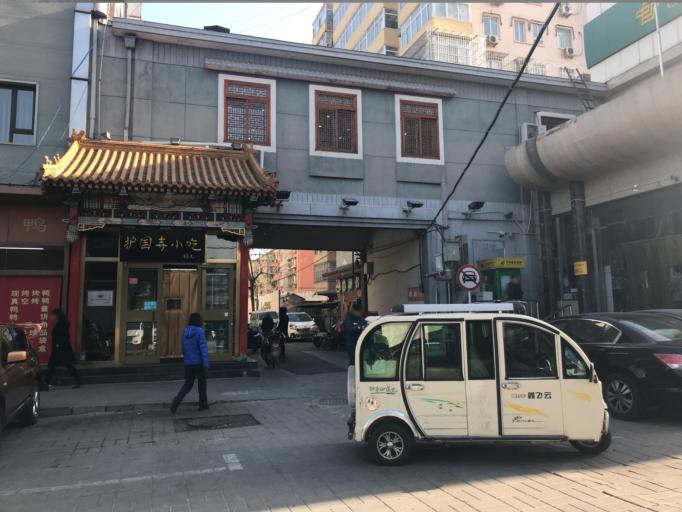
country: CN
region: Beijing
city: Beijing
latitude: 39.8982
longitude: 116.3794
